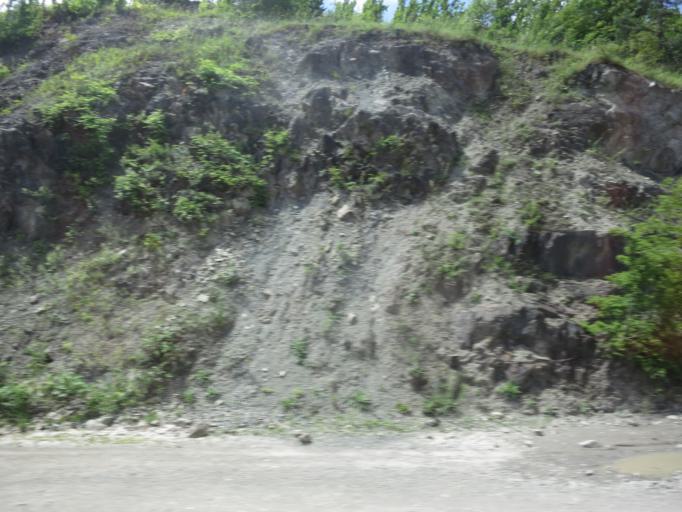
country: GE
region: Imereti
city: Kharagauli
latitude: 41.9694
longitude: 43.3158
